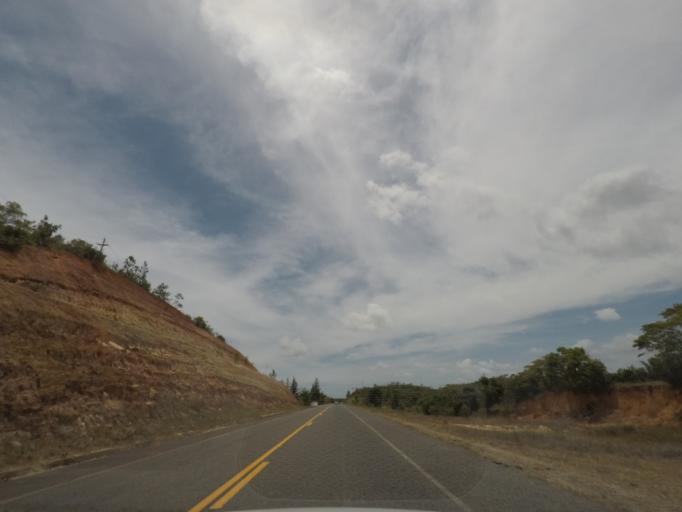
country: BR
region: Bahia
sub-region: Conde
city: Conde
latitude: -11.9014
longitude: -37.6525
